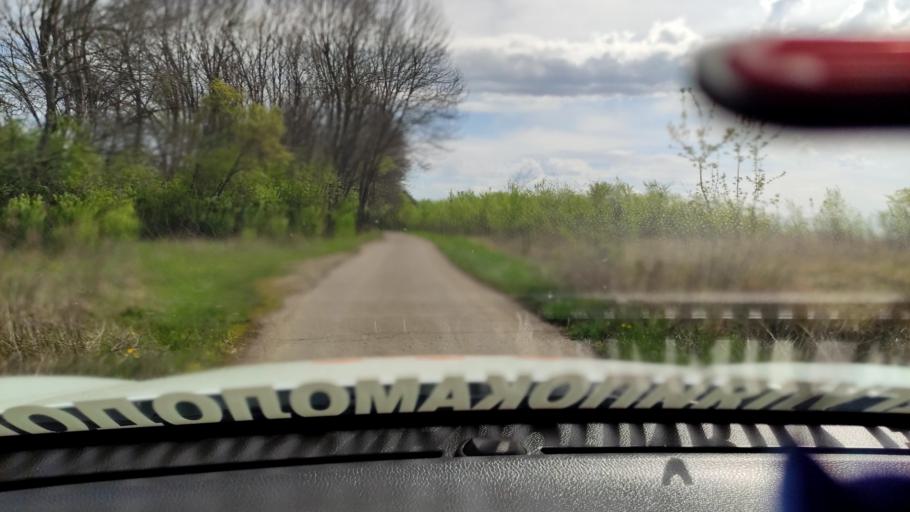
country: RU
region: Voronezj
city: Strelitsa
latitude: 51.5126
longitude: 38.9602
